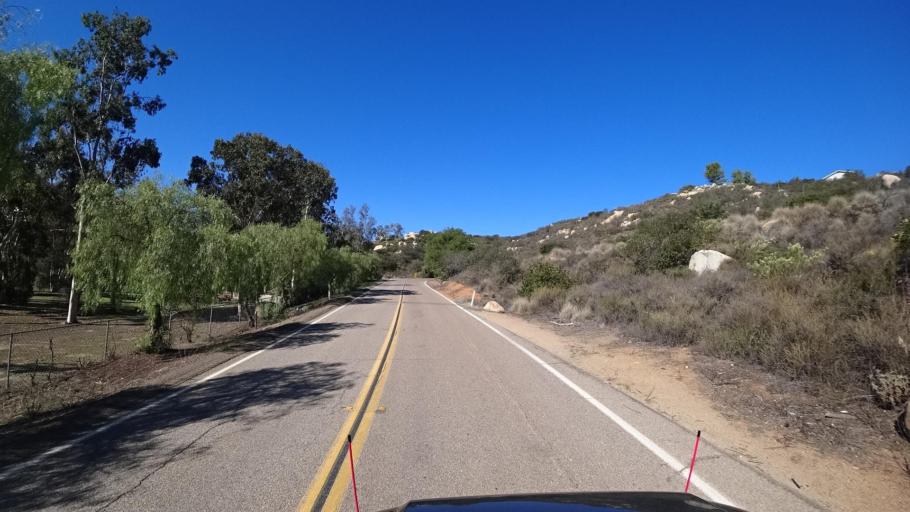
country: US
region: California
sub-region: San Diego County
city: Jamul
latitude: 32.7303
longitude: -116.8207
